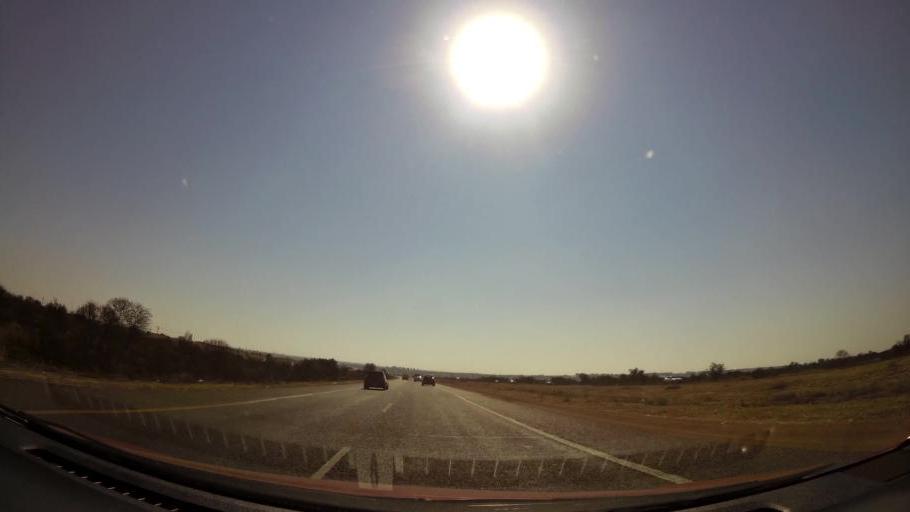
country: ZA
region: Gauteng
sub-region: City of Tshwane Metropolitan Municipality
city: Mabopane
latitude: -25.6067
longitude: 28.1138
